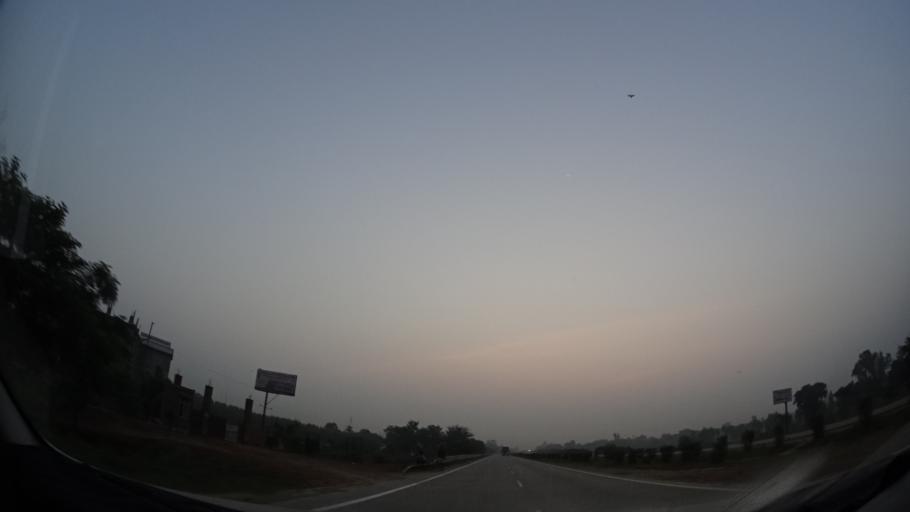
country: IN
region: Uttar Pradesh
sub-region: Bara Banki
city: Nawabganj
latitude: 26.9058
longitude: 81.1927
